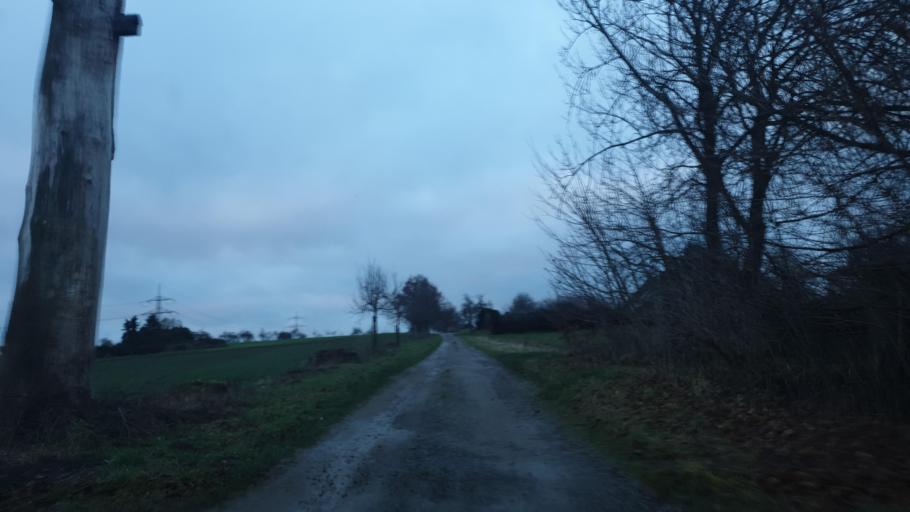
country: DE
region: North Rhine-Westphalia
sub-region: Regierungsbezirk Detmold
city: Hiddenhausen
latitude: 52.1429
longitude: 8.6324
